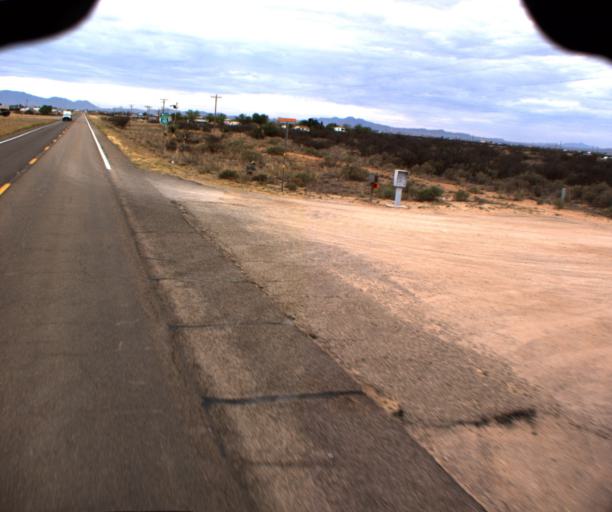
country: US
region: Arizona
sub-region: Cochise County
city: Willcox
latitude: 32.2825
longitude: -109.8118
